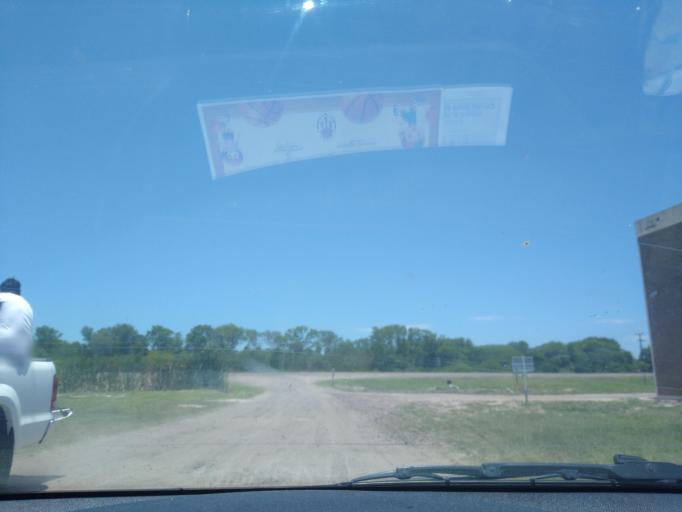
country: AR
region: Chaco
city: Makalle
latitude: -27.2525
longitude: -59.1646
